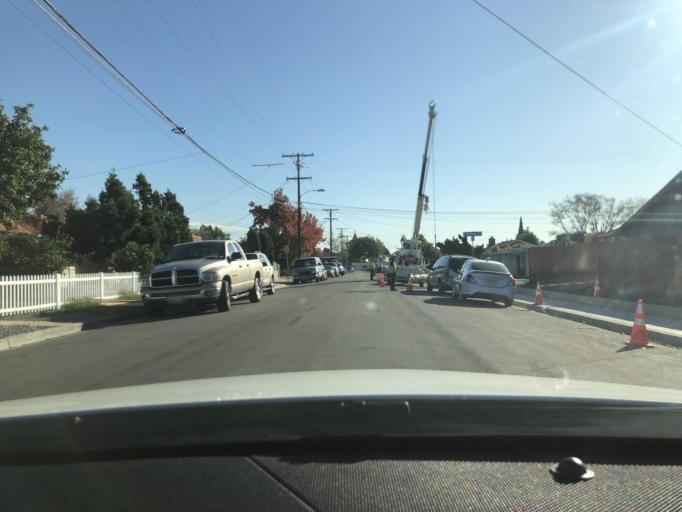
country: US
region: California
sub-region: San Diego County
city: Lemon Grove
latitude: 32.7443
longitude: -117.0585
